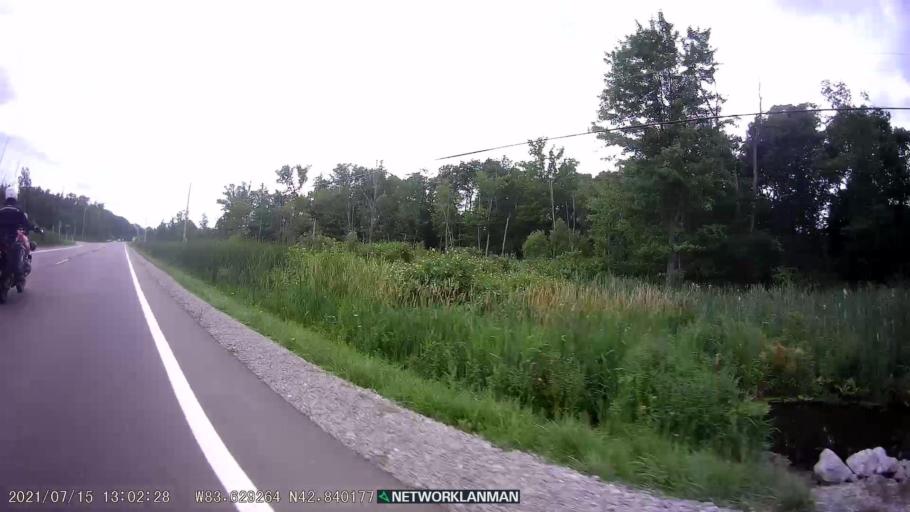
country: US
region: Michigan
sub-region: Oakland County
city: Holly
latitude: 42.8398
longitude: -83.6292
